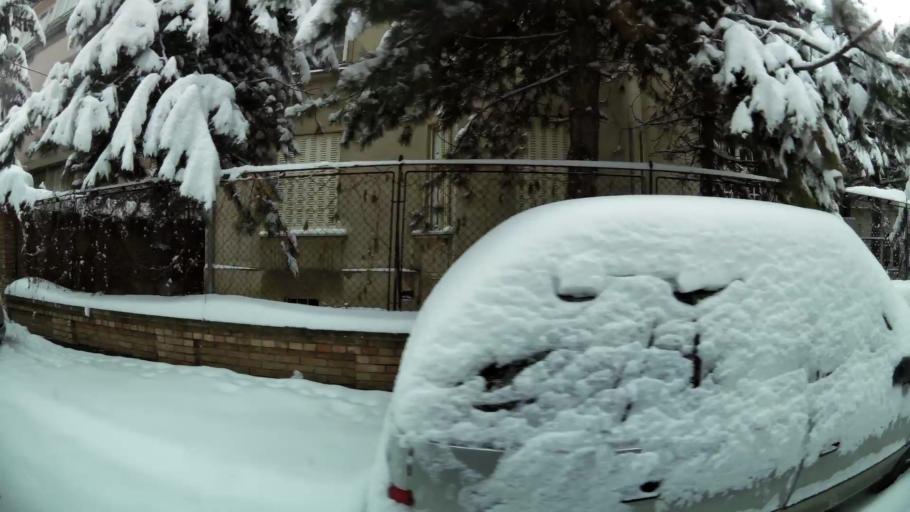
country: RS
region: Central Serbia
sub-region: Belgrade
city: Vracar
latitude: 44.7947
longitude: 20.4719
